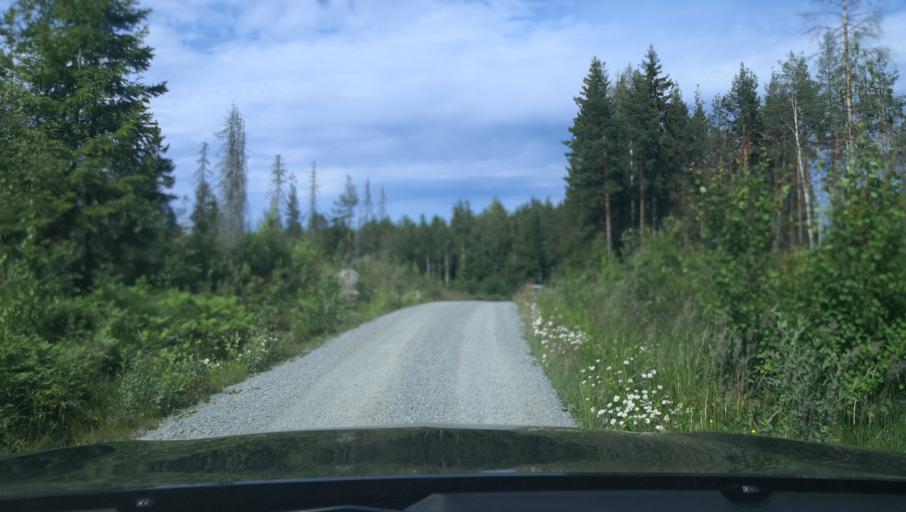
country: SE
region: Vaestmanland
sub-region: Surahammars Kommun
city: Ramnas
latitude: 59.9362
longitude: 16.1932
